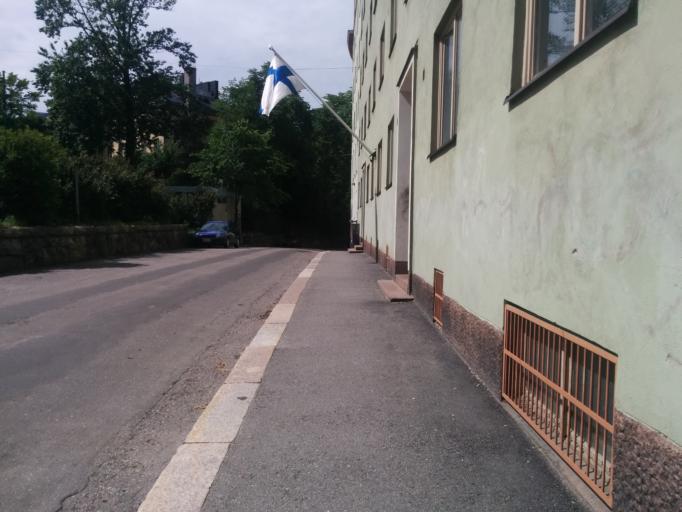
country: FI
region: Uusimaa
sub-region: Helsinki
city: Helsinki
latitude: 60.1863
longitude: 24.9586
